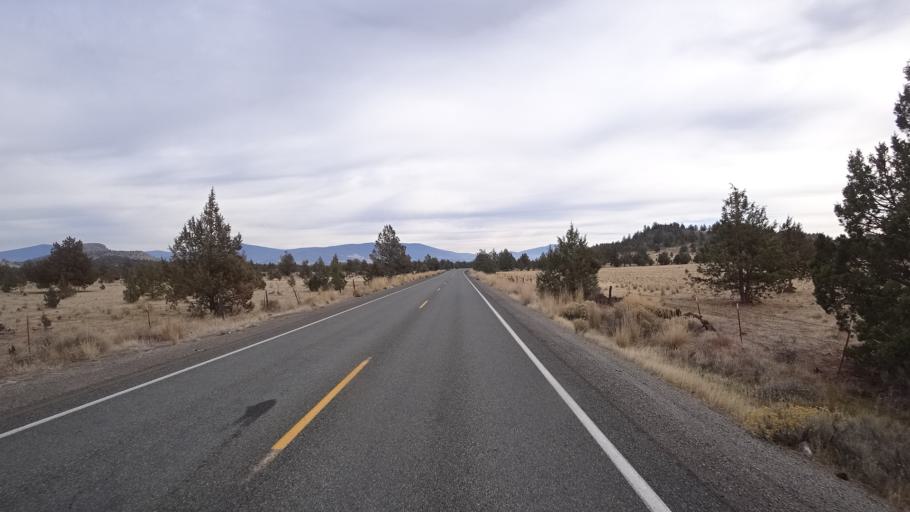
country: US
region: California
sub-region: Siskiyou County
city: Montague
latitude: 41.6392
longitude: -122.4624
